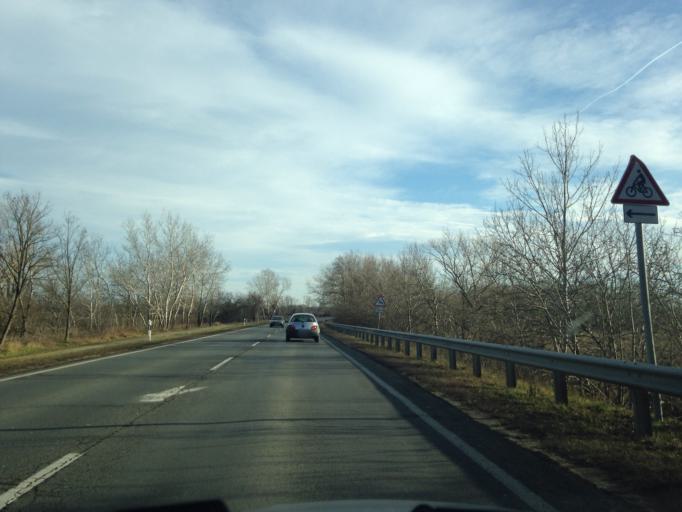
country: HU
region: Gyor-Moson-Sopron
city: Abda
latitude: 47.6871
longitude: 17.5630
